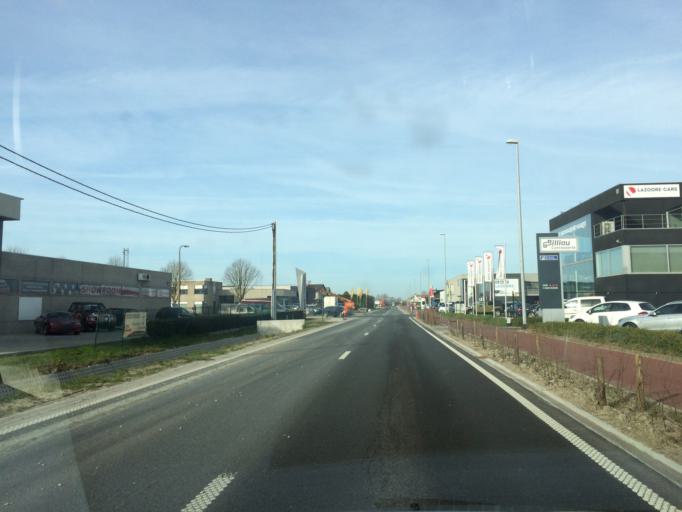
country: BE
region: Flanders
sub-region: Provincie West-Vlaanderen
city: Nieuwpoort
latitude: 51.1255
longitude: 2.7674
